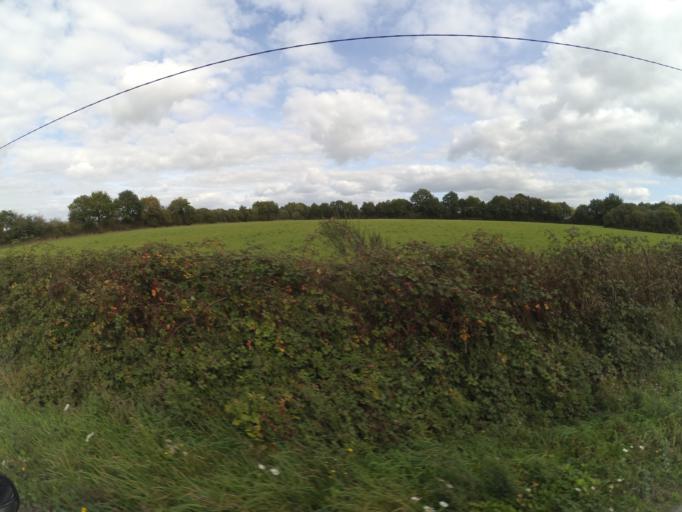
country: FR
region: Pays de la Loire
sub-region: Departement de la Loire-Atlantique
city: Fay-de-Bretagne
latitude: 47.4337
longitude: -1.8044
